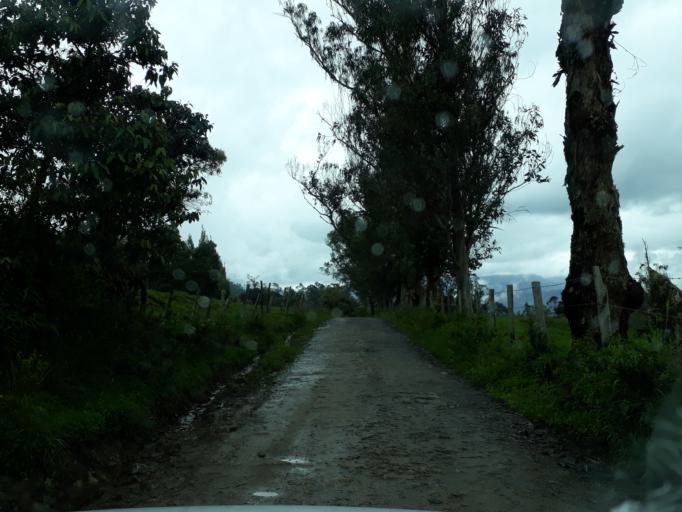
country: CO
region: Cundinamarca
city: Gacheta
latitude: 4.8669
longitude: -73.6335
